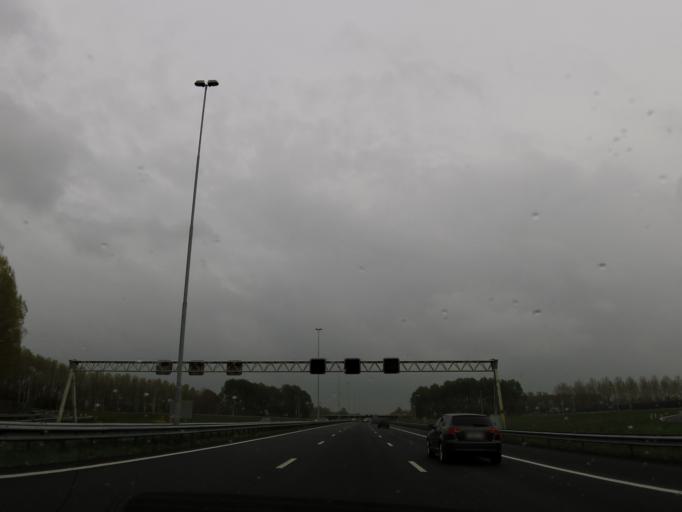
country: NL
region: North Brabant
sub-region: Gemeente Best
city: Best
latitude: 51.5254
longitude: 5.3915
